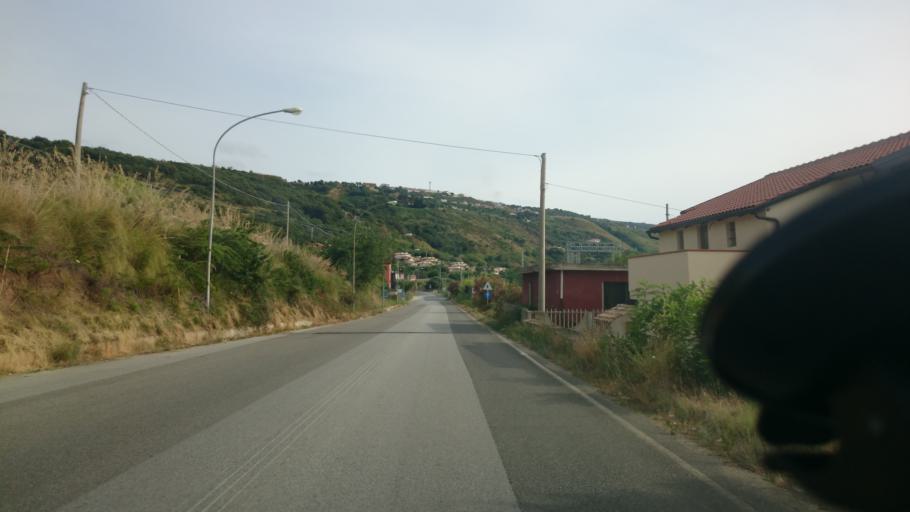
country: IT
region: Calabria
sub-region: Provincia di Vibo-Valentia
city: Zambrone
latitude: 38.7109
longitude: 15.9761
